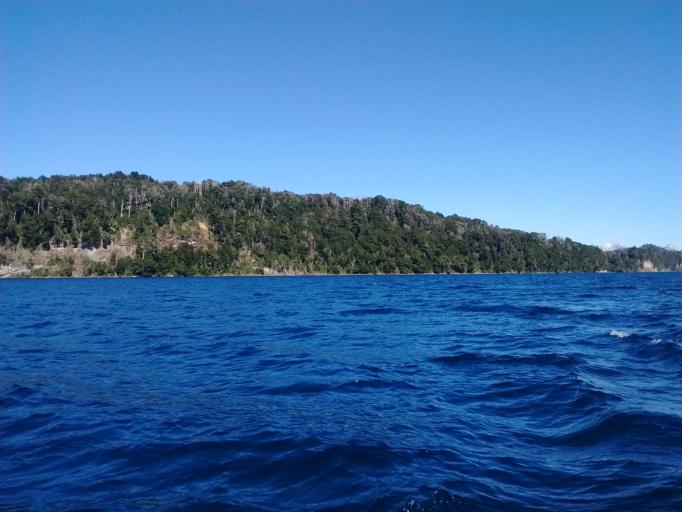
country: AR
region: Neuquen
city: Villa La Angostura
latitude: -40.8247
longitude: -71.6036
